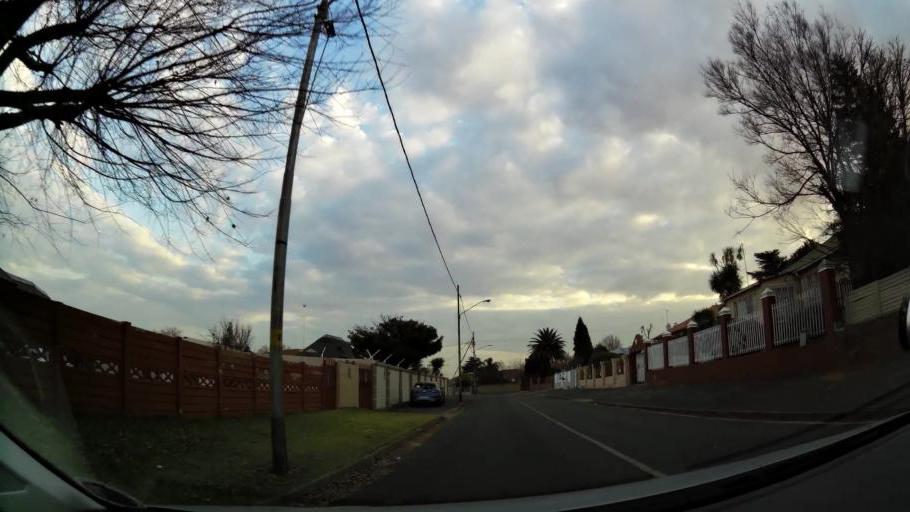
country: ZA
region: Gauteng
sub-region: Ekurhuleni Metropolitan Municipality
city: Germiston
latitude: -26.1896
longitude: 28.1515
